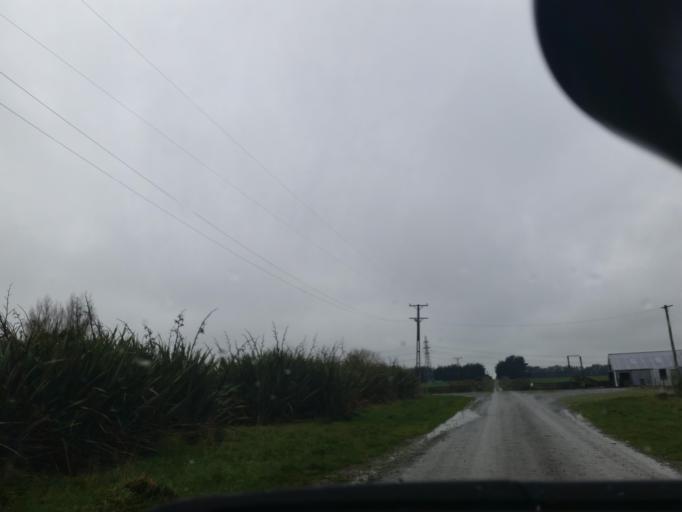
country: NZ
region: Southland
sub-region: Southland District
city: Winton
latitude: -46.1955
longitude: 168.1795
